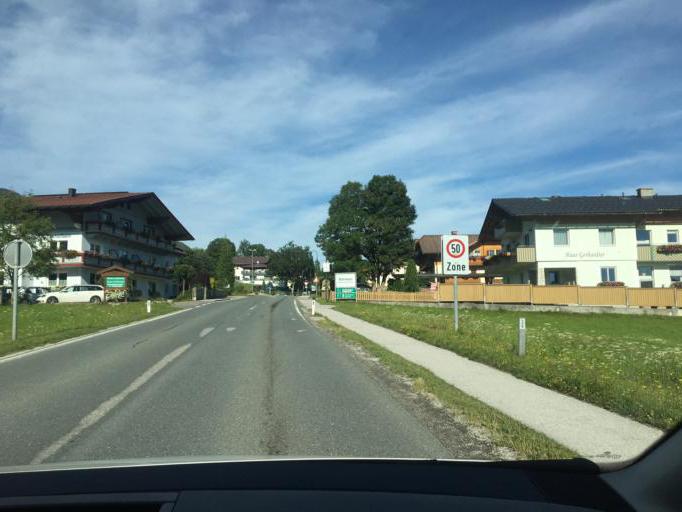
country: AT
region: Styria
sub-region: Politischer Bezirk Liezen
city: Schladming
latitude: 47.3835
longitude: 13.6748
